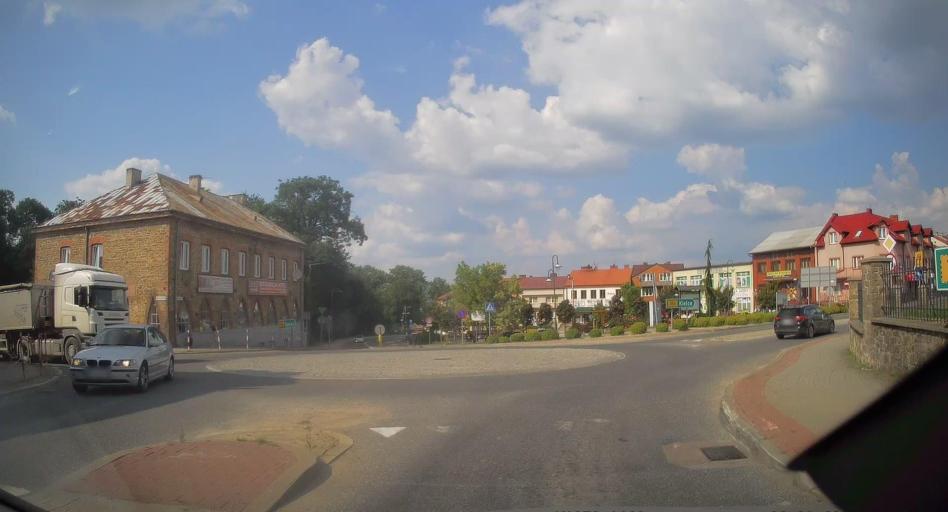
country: PL
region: Swietokrzyskie
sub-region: Powiat kielecki
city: Lopuszno
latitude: 50.9483
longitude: 20.2505
